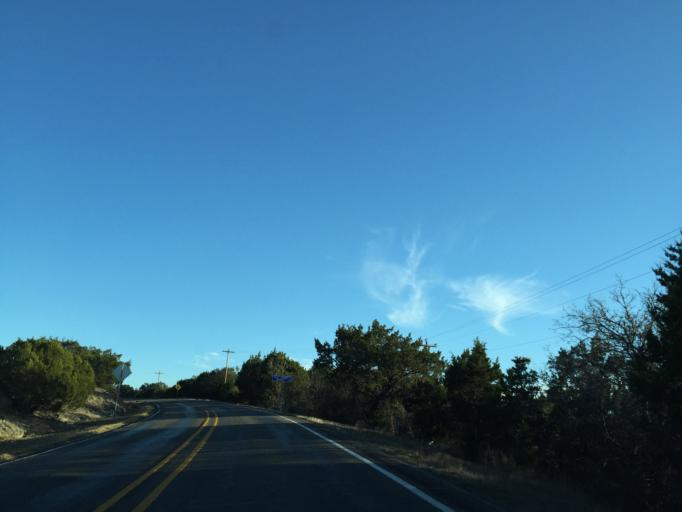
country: US
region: Texas
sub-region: Travis County
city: Lago Vista
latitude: 30.5123
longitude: -98.0408
